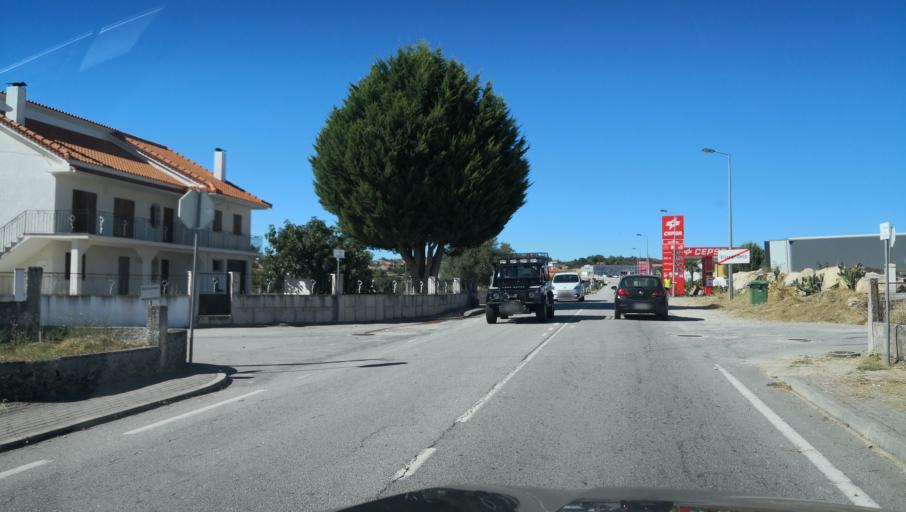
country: PT
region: Vila Real
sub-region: Valpacos
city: Valpacos
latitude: 41.6681
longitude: -7.3363
